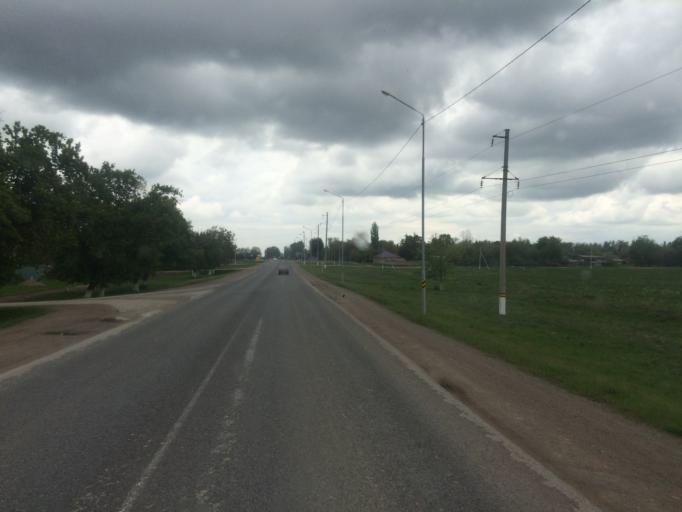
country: KZ
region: Zhambyl
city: Georgiyevka
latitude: 43.1449
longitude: 74.6138
